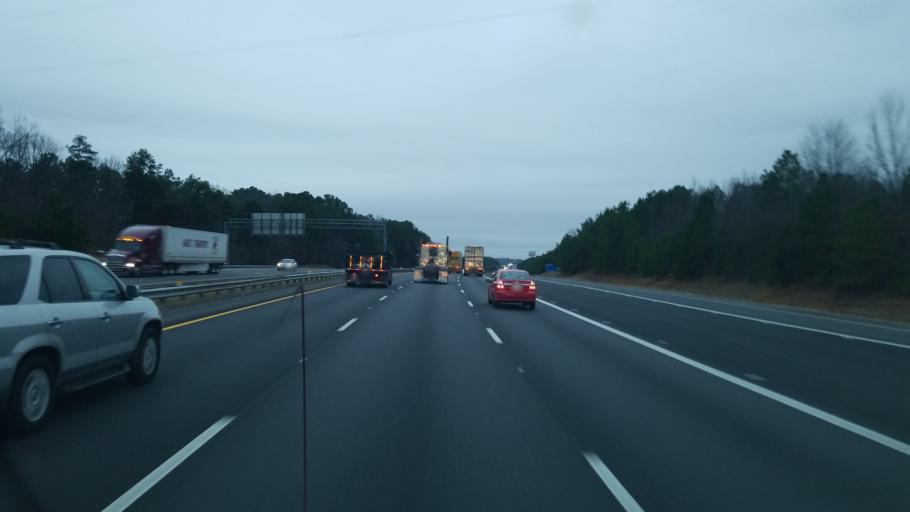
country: US
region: Georgia
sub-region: Gordon County
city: Calhoun
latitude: 34.5347
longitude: -84.9218
